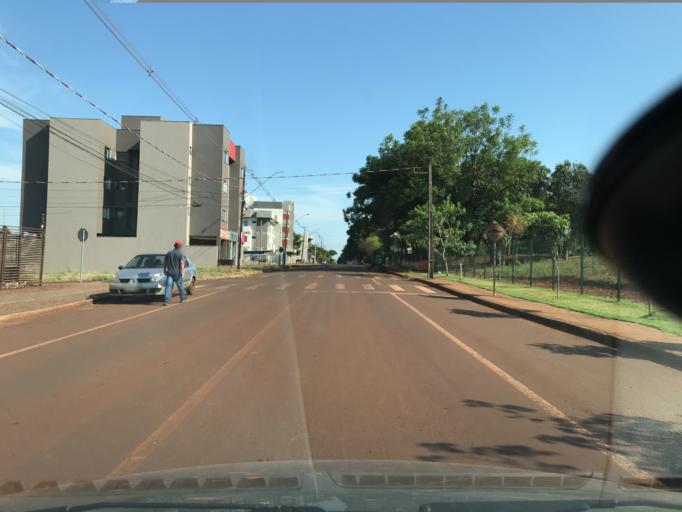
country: BR
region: Parana
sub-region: Palotina
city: Palotina
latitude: -24.2972
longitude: -53.8429
